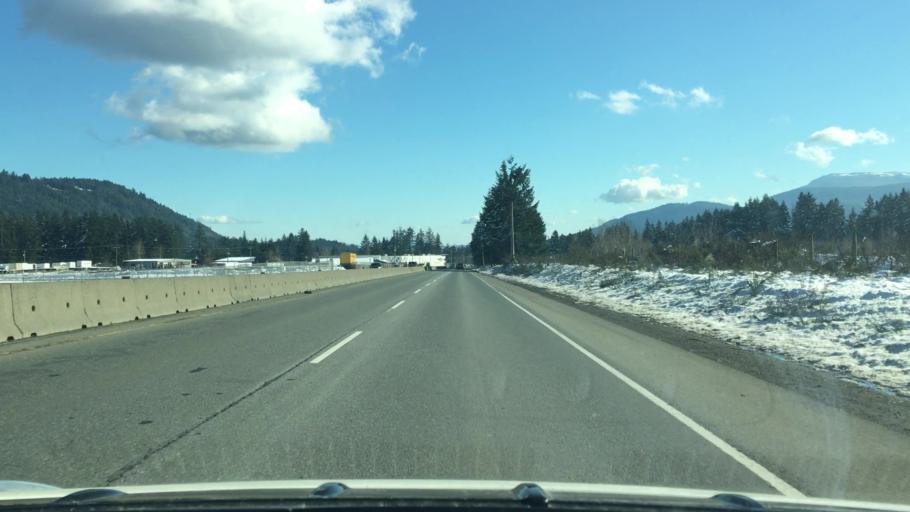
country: CA
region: British Columbia
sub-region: Cowichan Valley Regional District
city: Ladysmith
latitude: 49.0422
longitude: -123.8696
